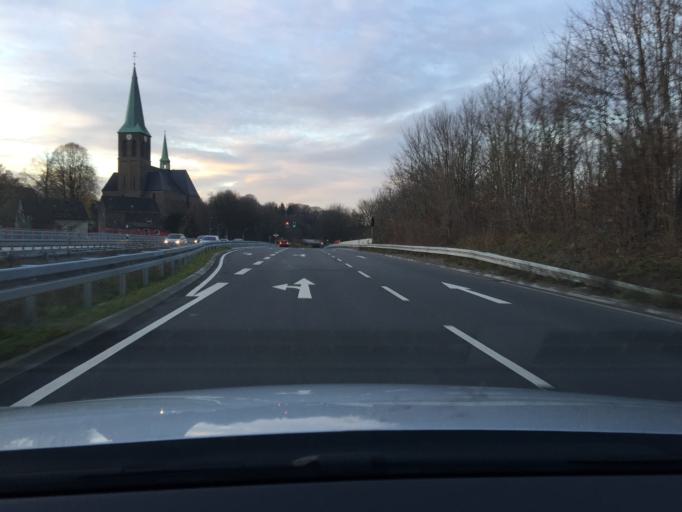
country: DE
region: North Rhine-Westphalia
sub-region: Regierungsbezirk Dusseldorf
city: Velbert
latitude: 51.3837
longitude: 7.0863
